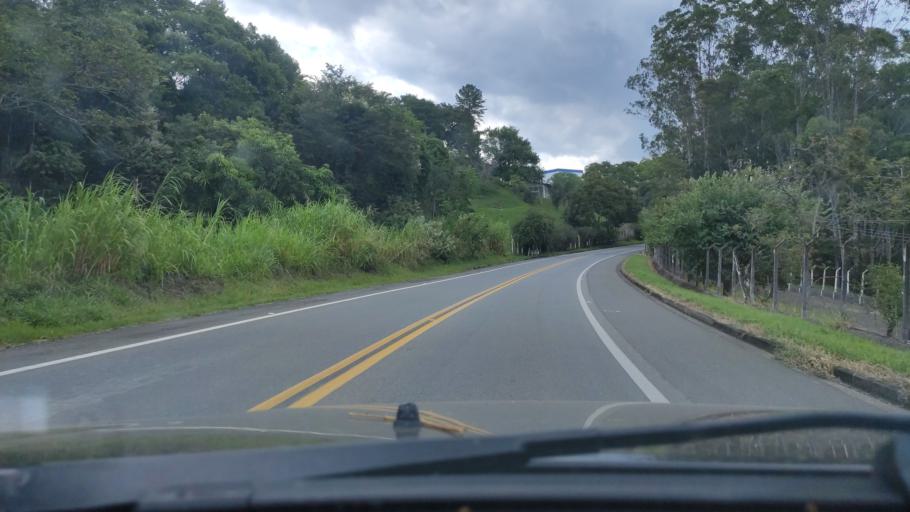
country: BR
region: Sao Paulo
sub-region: Aguas De Lindoia
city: Aguas de Lindoia
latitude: -22.4723
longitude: -46.7109
